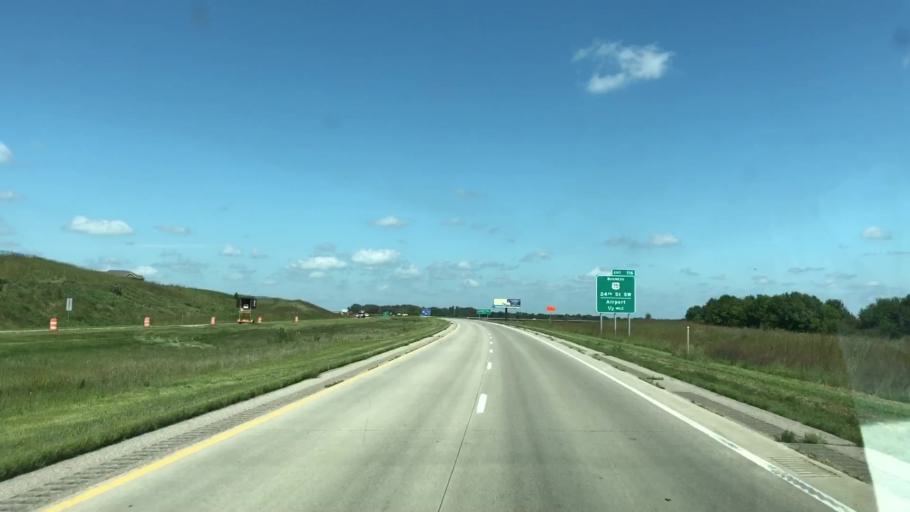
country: US
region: Iowa
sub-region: Plymouth County
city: Le Mars
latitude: 42.7515
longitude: -96.2104
